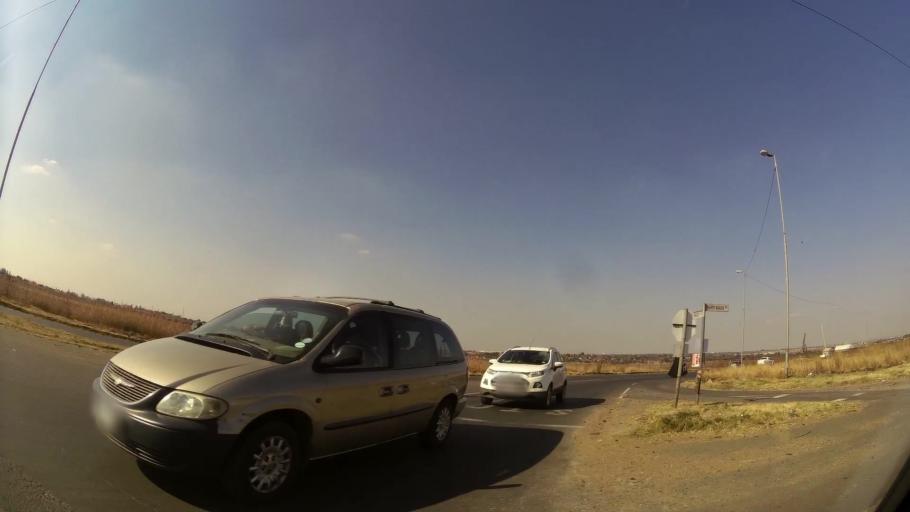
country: ZA
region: Gauteng
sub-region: Ekurhuleni Metropolitan Municipality
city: Boksburg
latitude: -26.2353
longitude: 28.2958
